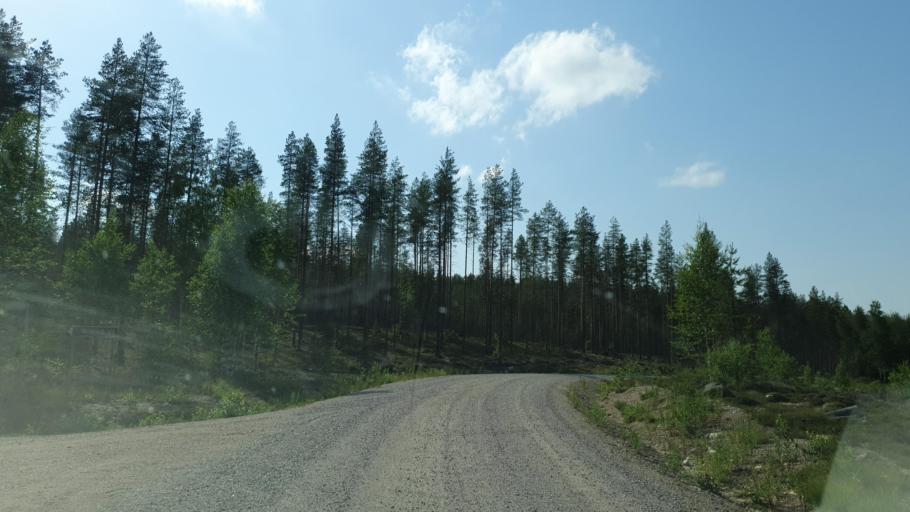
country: FI
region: Kainuu
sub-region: Kehys-Kainuu
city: Kuhmo
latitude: 64.0174
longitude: 29.9103
